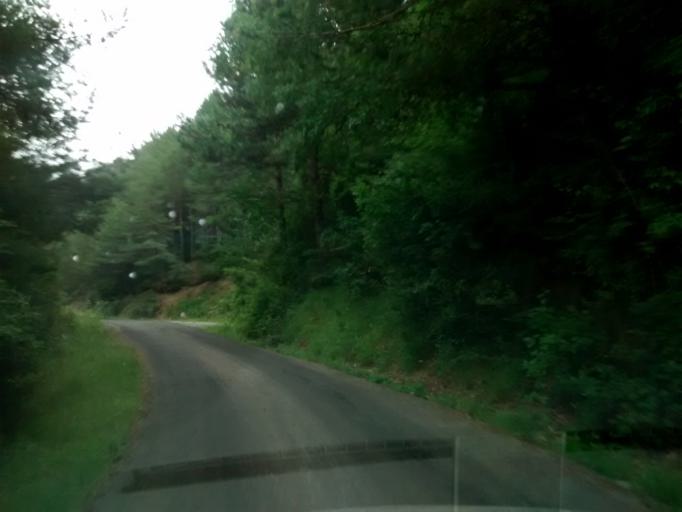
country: ES
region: Aragon
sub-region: Provincia de Huesca
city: Puertolas
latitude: 42.5634
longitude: 0.1394
